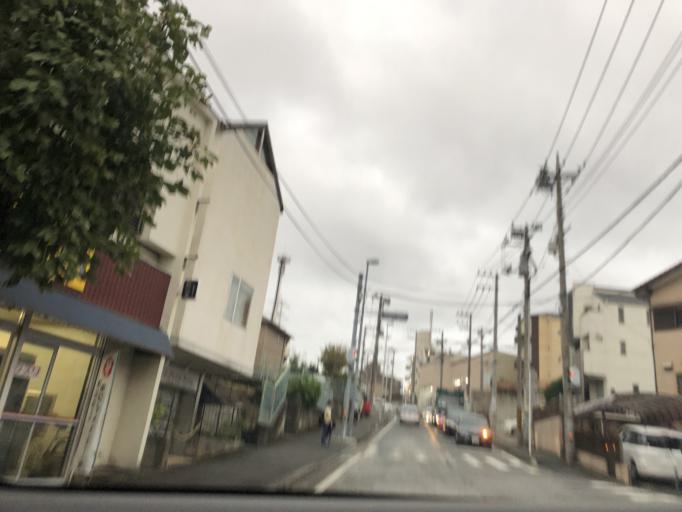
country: JP
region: Kanagawa
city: Yokohama
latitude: 35.5169
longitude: 139.6474
